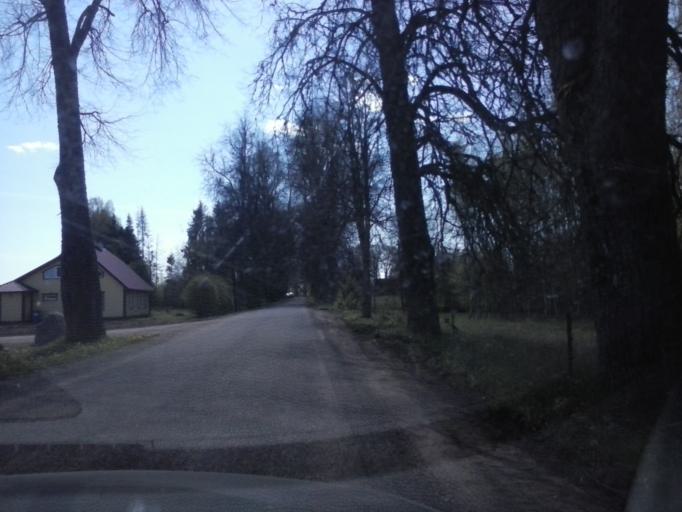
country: EE
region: Valgamaa
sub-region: Torva linn
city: Torva
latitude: 58.2304
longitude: 25.8902
